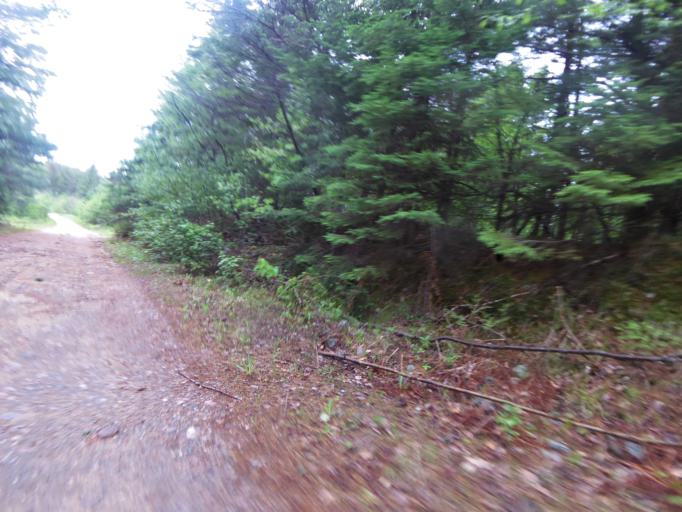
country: CA
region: Quebec
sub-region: Outaouais
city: Shawville
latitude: 45.9103
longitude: -76.2983
